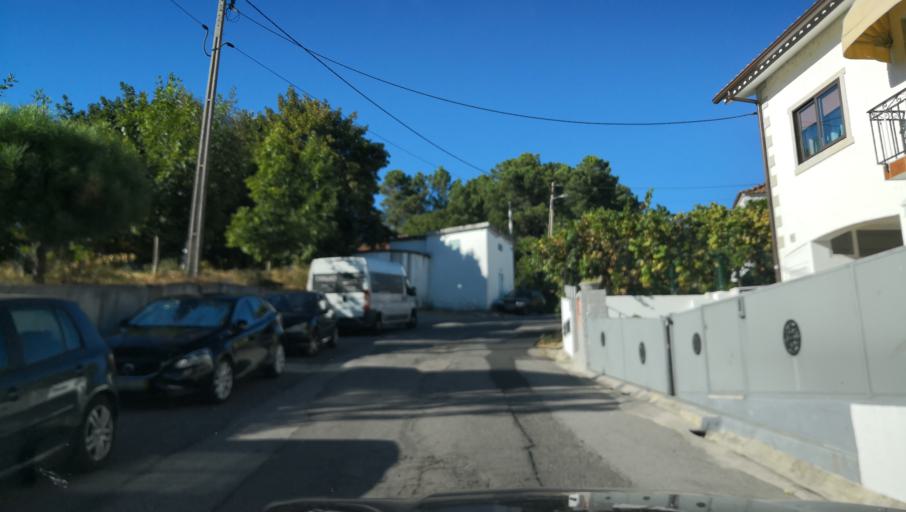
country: PT
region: Vila Real
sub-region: Vila Real
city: Vila Real
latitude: 41.3222
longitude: -7.7691
